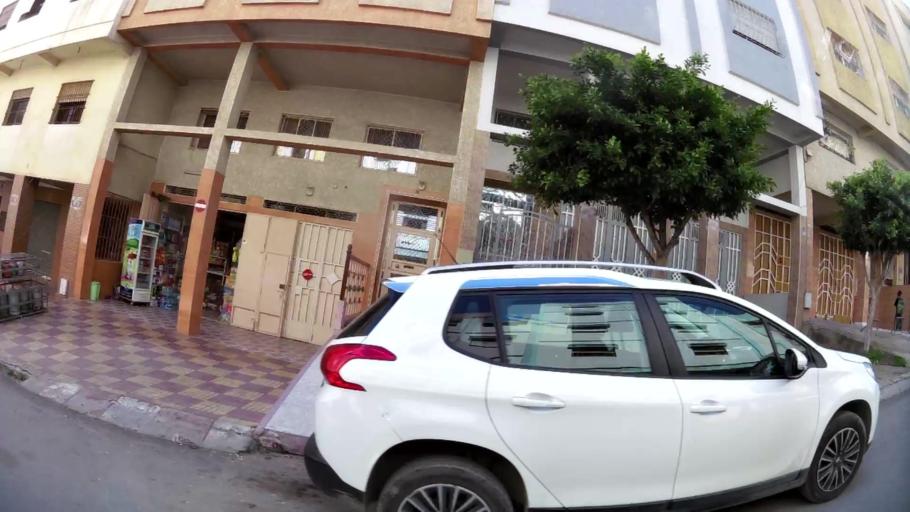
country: MA
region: Tanger-Tetouan
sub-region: Tanger-Assilah
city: Tangier
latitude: 35.7580
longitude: -5.8063
